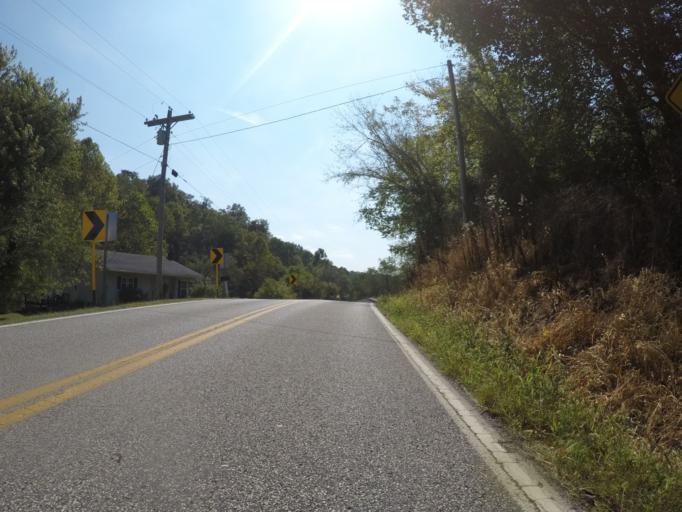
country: US
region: West Virginia
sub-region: Cabell County
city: Lesage
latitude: 38.5648
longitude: -82.3968
